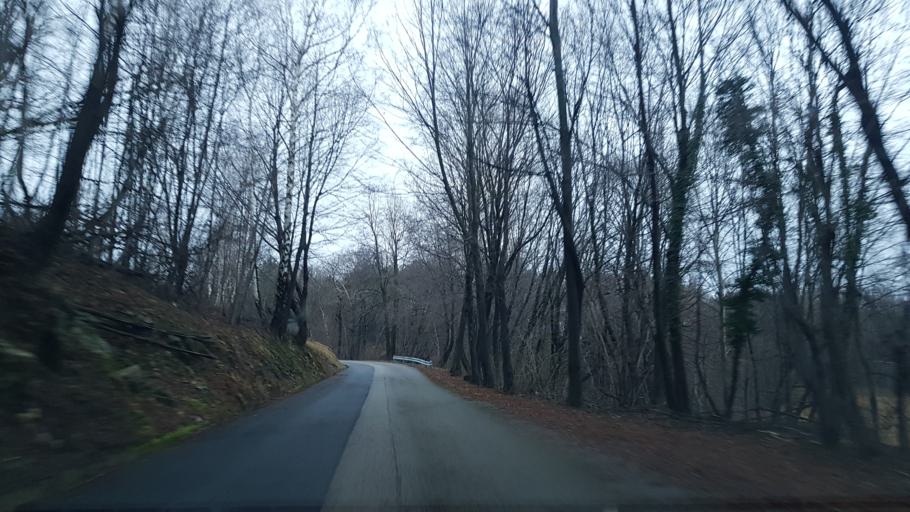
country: IT
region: Friuli Venezia Giulia
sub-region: Provincia di Udine
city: Stregna
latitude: 46.1096
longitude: 13.5813
